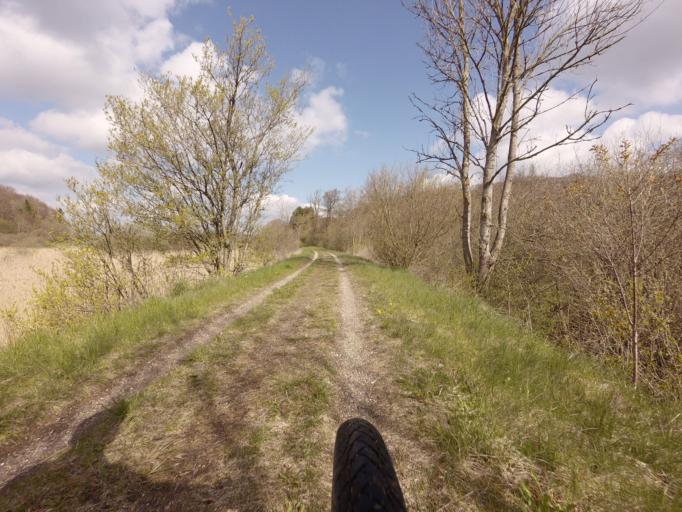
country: DK
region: North Denmark
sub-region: Mariagerfjord Kommune
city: Hadsund
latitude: 56.6858
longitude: 10.1052
